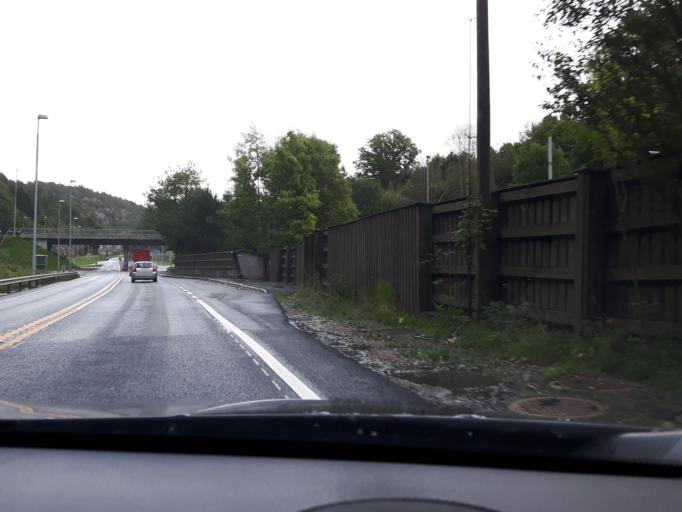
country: NO
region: Vest-Agder
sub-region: Songdalen
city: Nodeland
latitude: 58.1445
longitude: 7.8811
